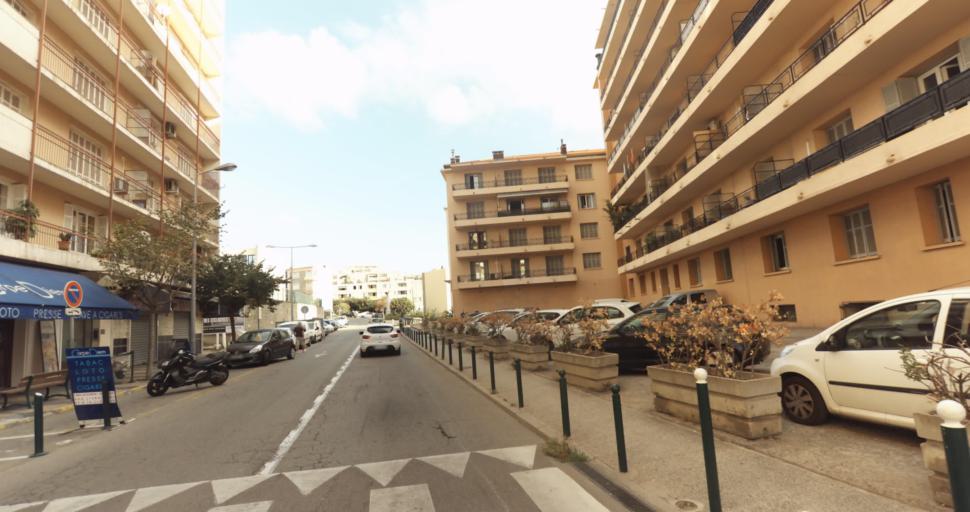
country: FR
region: Corsica
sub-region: Departement de la Corse-du-Sud
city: Ajaccio
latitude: 41.9296
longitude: 8.7374
